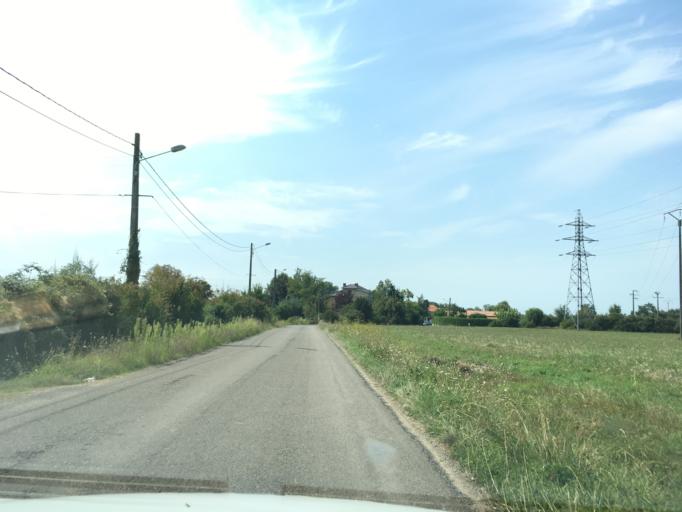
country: FR
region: Midi-Pyrenees
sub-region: Departement du Tarn-et-Garonne
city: Montauban
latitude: 44.0090
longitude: 1.3381
